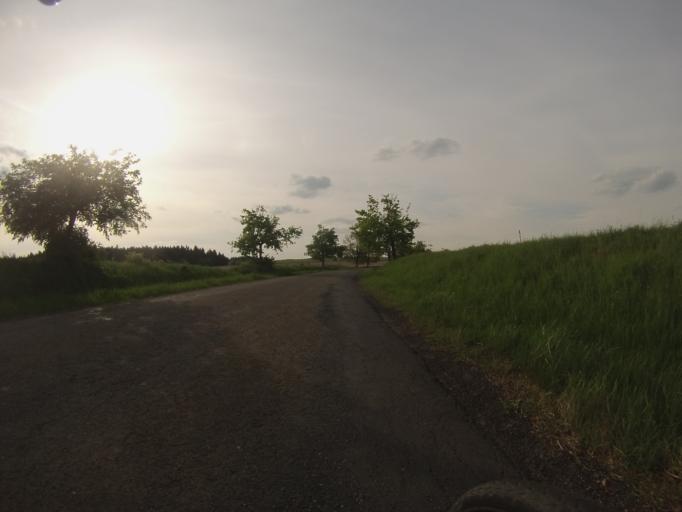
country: CZ
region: Olomoucky
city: Protivanov
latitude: 49.4604
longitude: 16.8702
